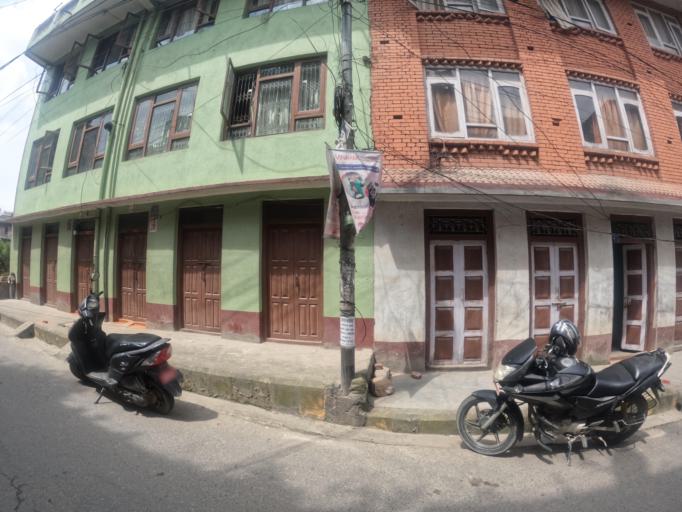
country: NP
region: Central Region
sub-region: Bagmati Zone
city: Bhaktapur
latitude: 27.6822
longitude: 85.3832
